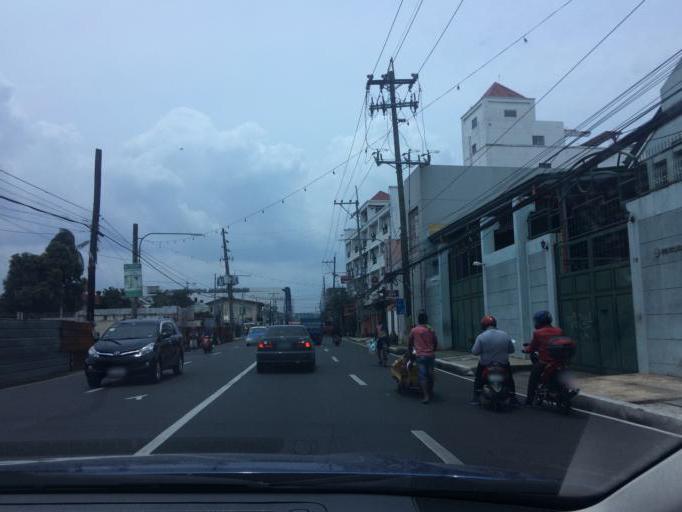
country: PH
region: Metro Manila
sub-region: Makati City
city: Makati City
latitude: 14.5251
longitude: 120.9970
